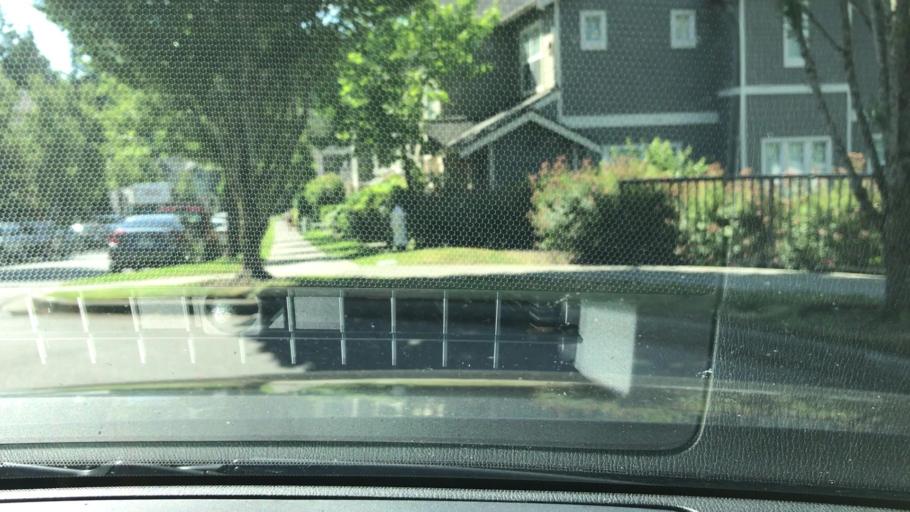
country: US
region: Washington
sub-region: King County
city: Issaquah
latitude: 47.5307
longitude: -122.0716
